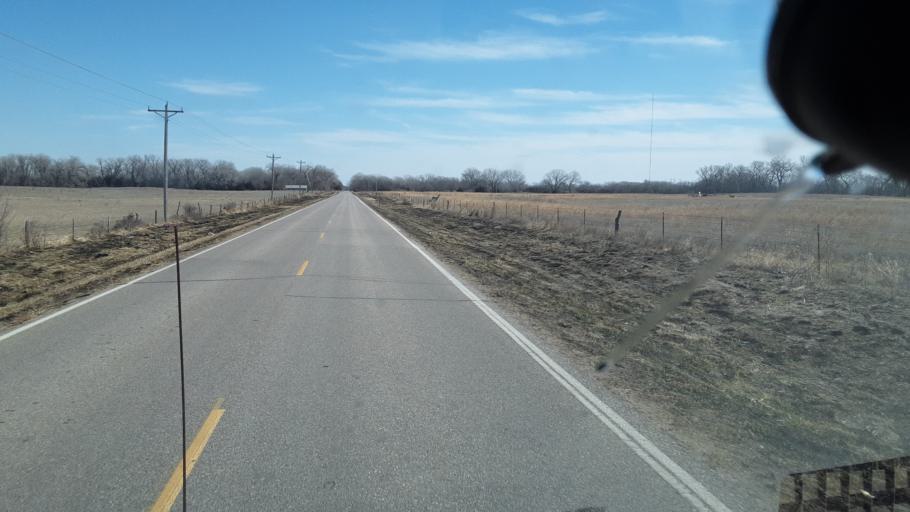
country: US
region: Kansas
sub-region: Reno County
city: Hutchinson
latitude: 38.1593
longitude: -97.8927
